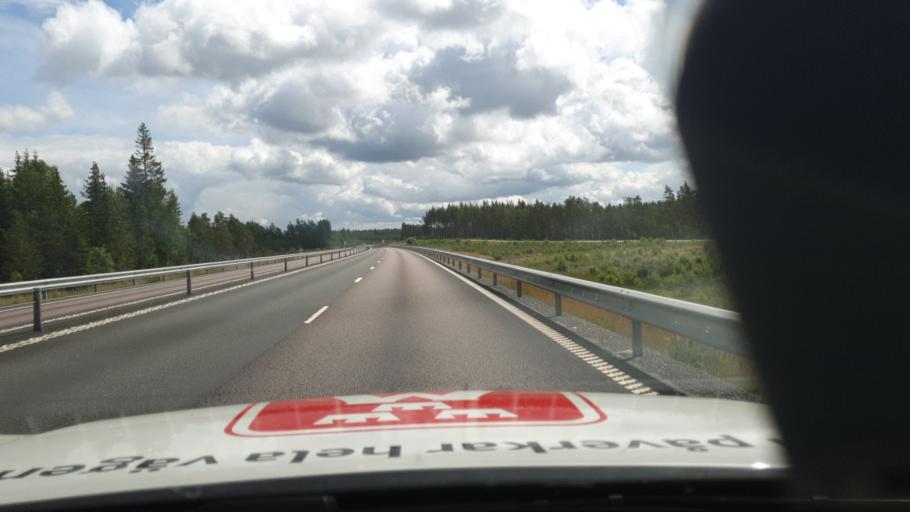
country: SE
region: Joenkoeping
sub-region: Mullsjo Kommun
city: Mullsjoe
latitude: 57.8658
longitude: 13.9707
